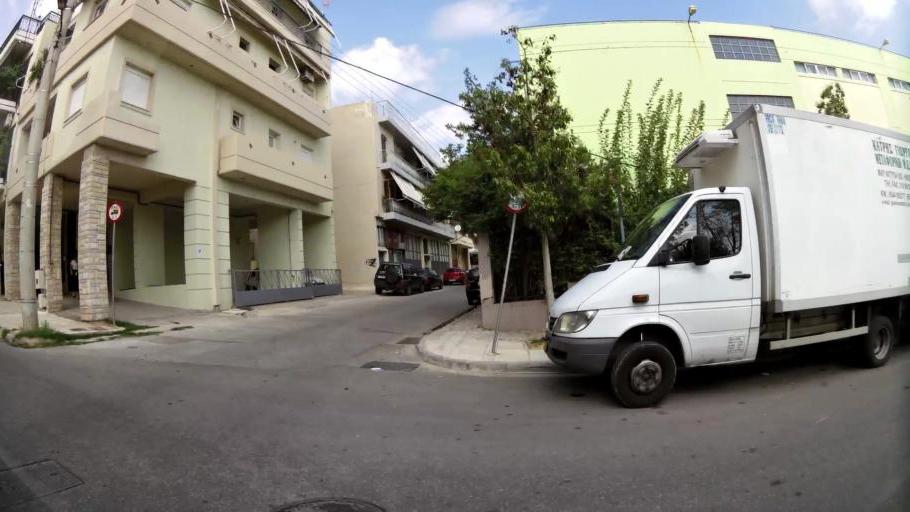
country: GR
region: Attica
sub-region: Nomarchia Athinas
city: Petroupolis
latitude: 38.0445
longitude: 23.6962
